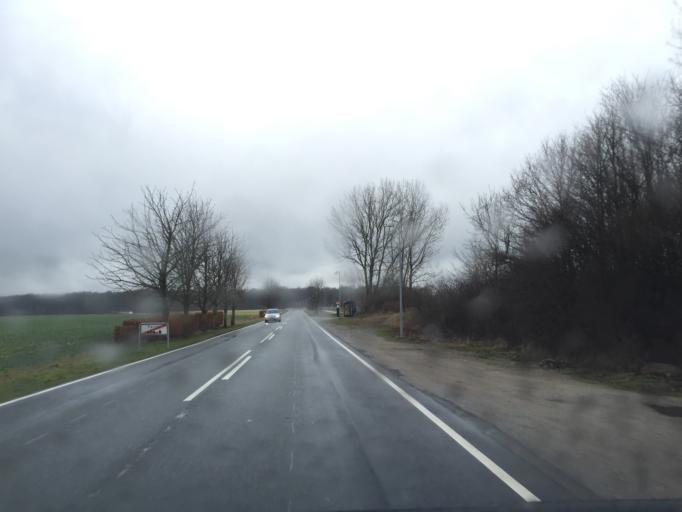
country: DK
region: Capital Region
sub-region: Fureso Kommune
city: Farum
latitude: 55.8154
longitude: 12.3434
